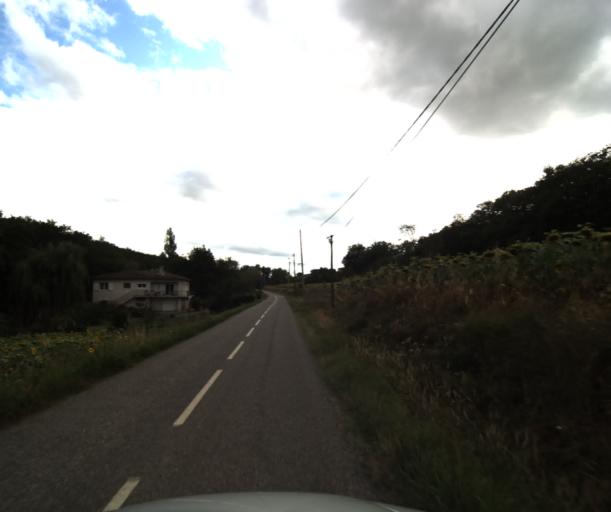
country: FR
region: Midi-Pyrenees
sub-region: Departement de la Haute-Garonne
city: Eaunes
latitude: 43.4177
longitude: 1.3416
